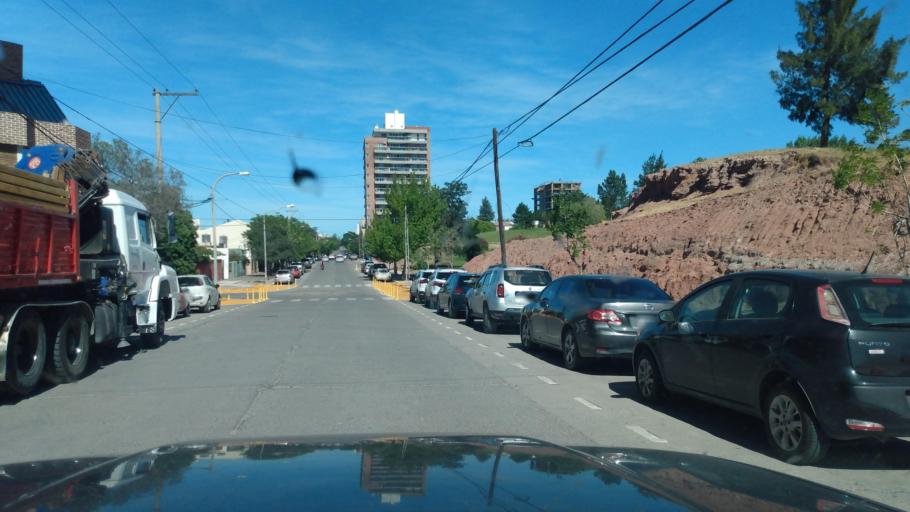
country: AR
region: Neuquen
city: Neuquen
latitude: -38.9475
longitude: -68.0642
